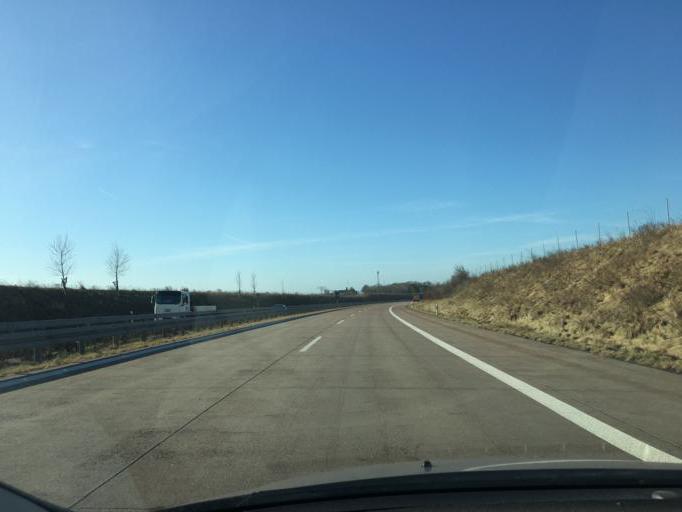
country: DE
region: Saxony
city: Narsdorf
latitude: 50.9778
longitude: 12.6966
